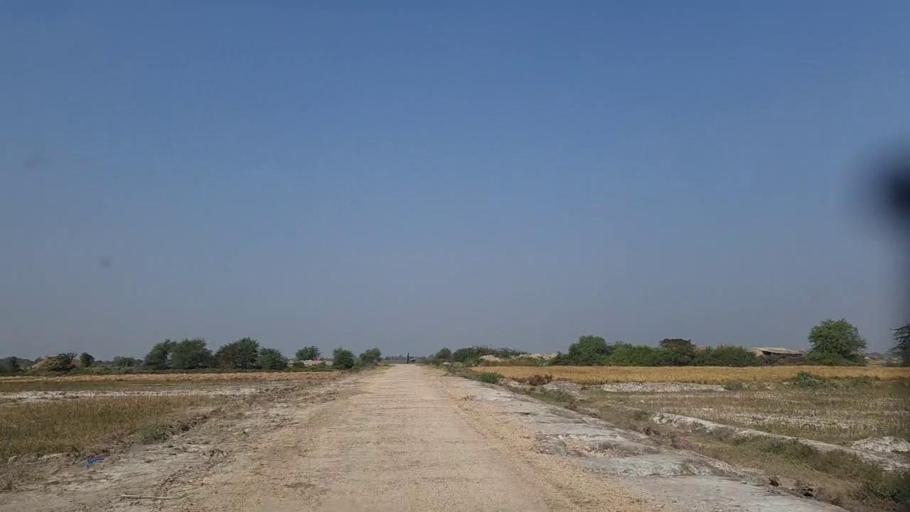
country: PK
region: Sindh
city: Mirpur Batoro
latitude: 24.5849
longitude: 68.1365
